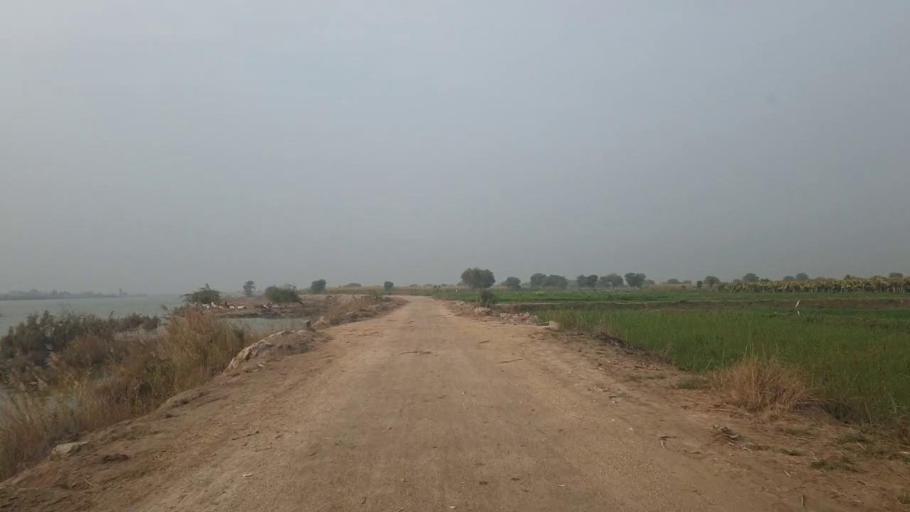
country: PK
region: Sindh
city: Berani
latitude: 25.8165
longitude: 68.7380
